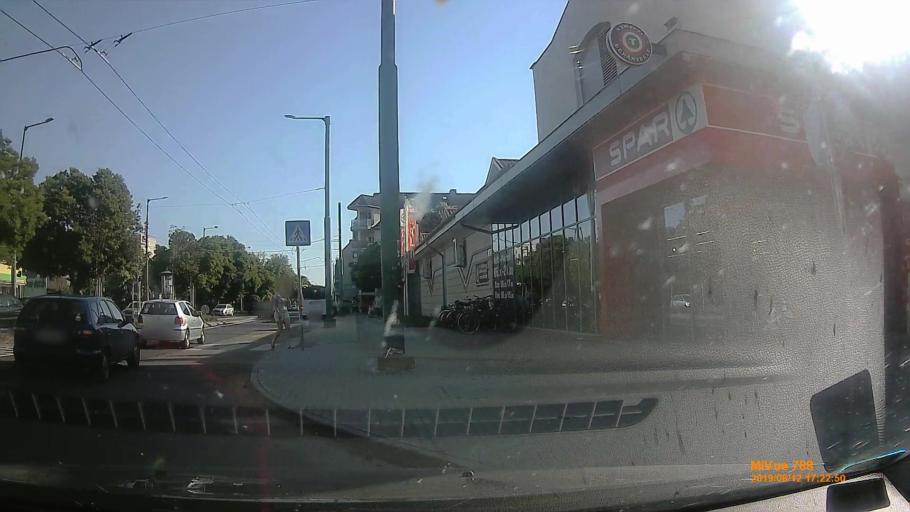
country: HU
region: Csongrad
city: Szeged
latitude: 46.2639
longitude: 20.1645
